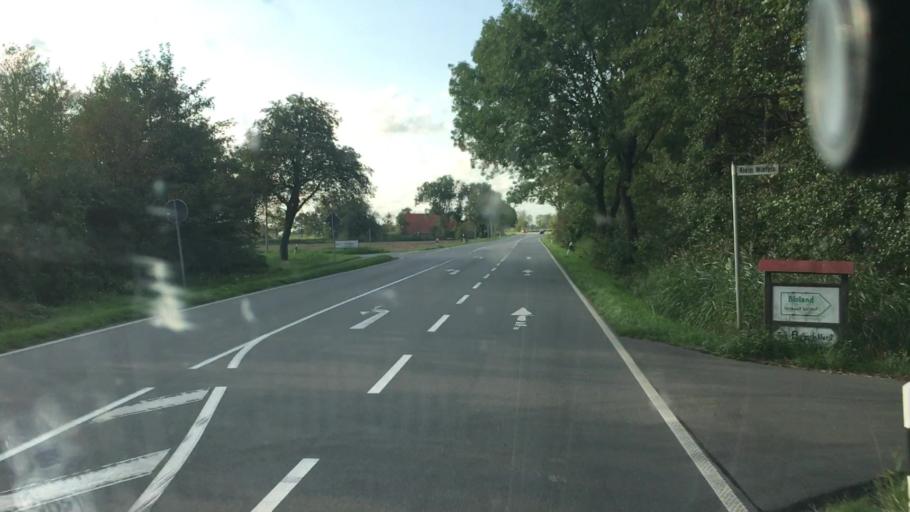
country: DE
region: Lower Saxony
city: Jever
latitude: 53.5907
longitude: 7.8731
